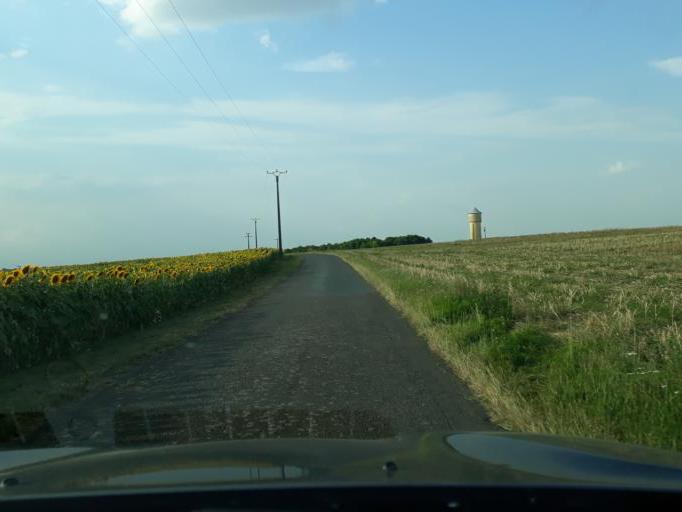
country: FR
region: Centre
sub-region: Departement du Loir-et-Cher
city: Ouzouer-le-Marche
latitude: 47.8104
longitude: 1.4951
